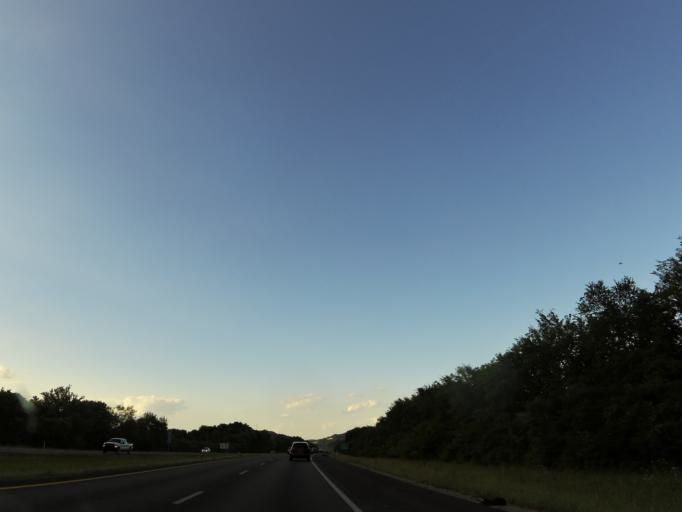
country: US
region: Tennessee
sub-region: Williamson County
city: Thompson's Station
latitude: 35.7945
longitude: -86.8590
